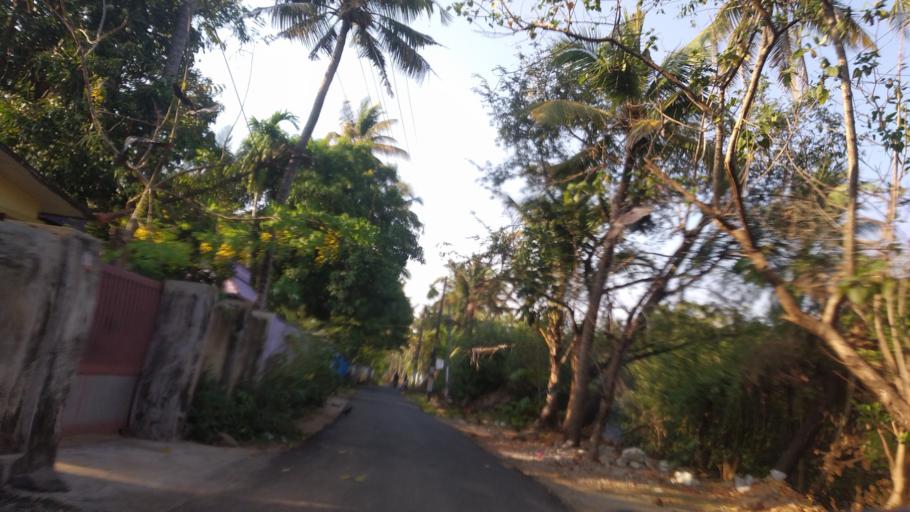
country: IN
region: Kerala
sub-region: Thrissur District
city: Kodungallur
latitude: 10.1337
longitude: 76.2017
